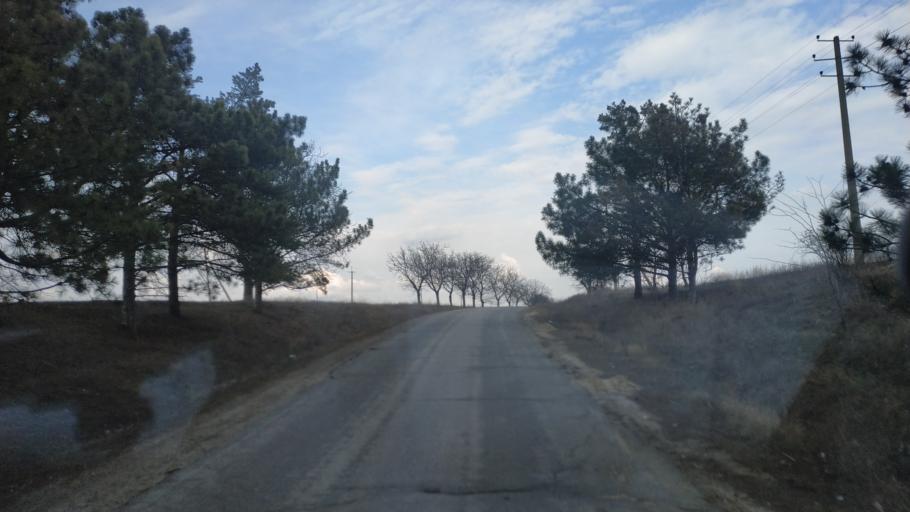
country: MD
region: Anenii Noi
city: Anenii Noi
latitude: 46.9091
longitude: 29.3244
